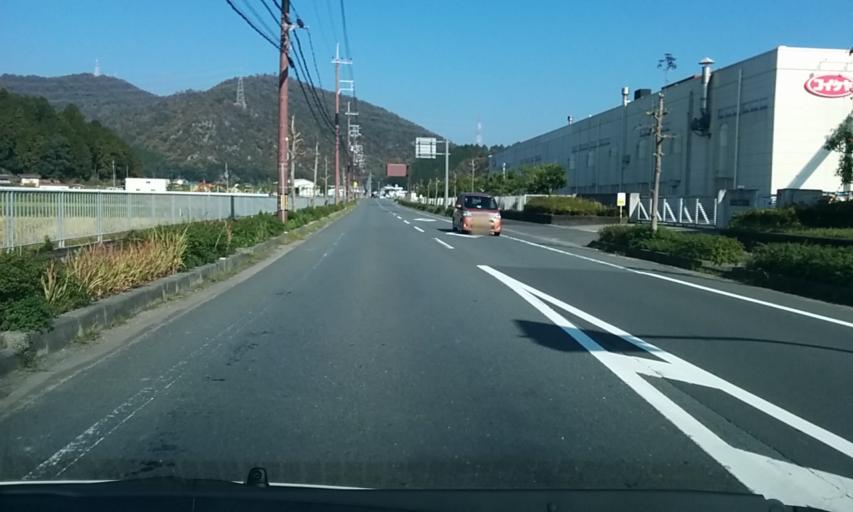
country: JP
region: Kyoto
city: Kameoka
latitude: 35.1261
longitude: 135.4830
